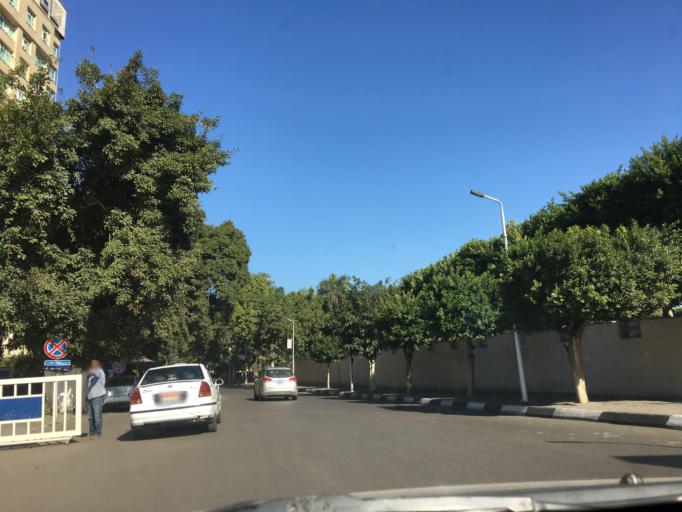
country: EG
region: Muhafazat al Qahirah
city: Cairo
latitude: 30.0440
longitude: 31.2271
